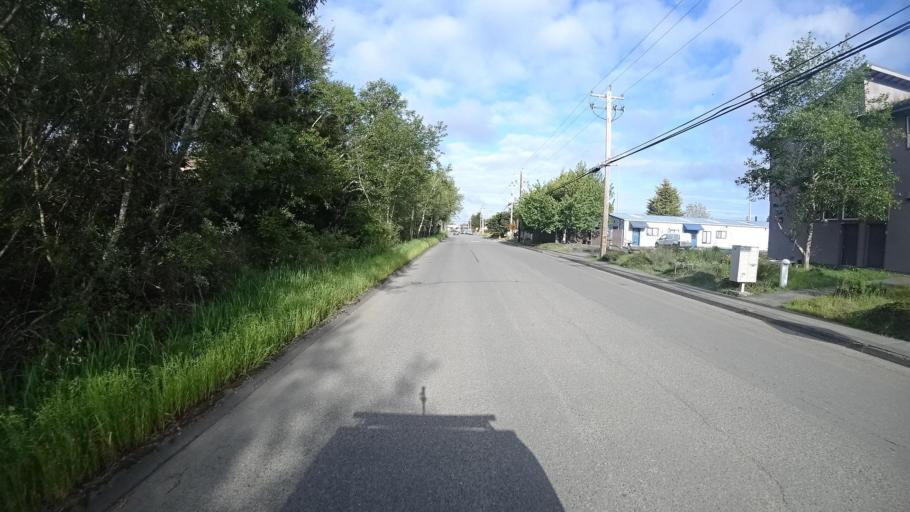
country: US
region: California
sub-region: Humboldt County
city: Arcata
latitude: 40.9012
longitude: -124.0698
